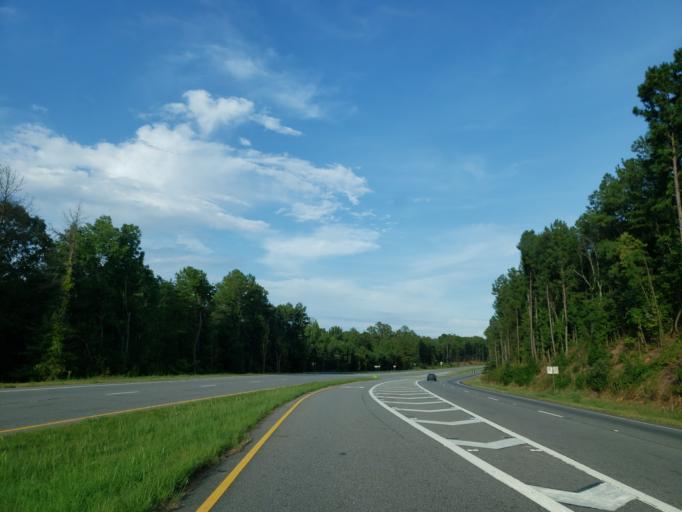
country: US
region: Georgia
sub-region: Bartow County
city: Euharlee
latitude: 34.2112
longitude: -84.9707
